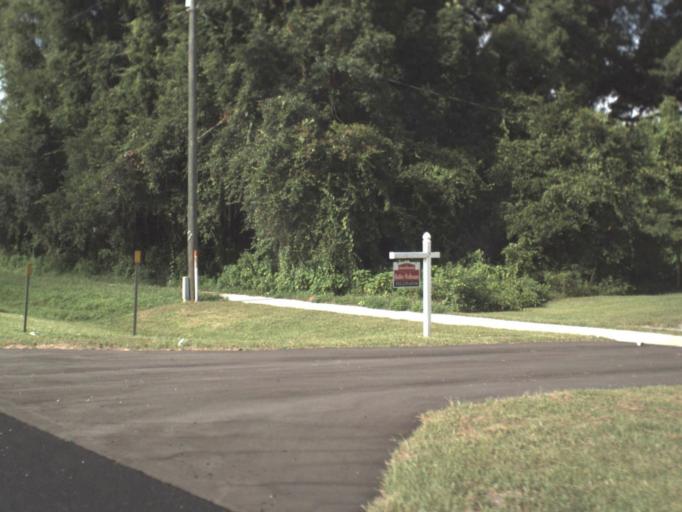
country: US
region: Florida
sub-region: Pasco County
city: Dade City North
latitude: 28.3868
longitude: -82.1937
